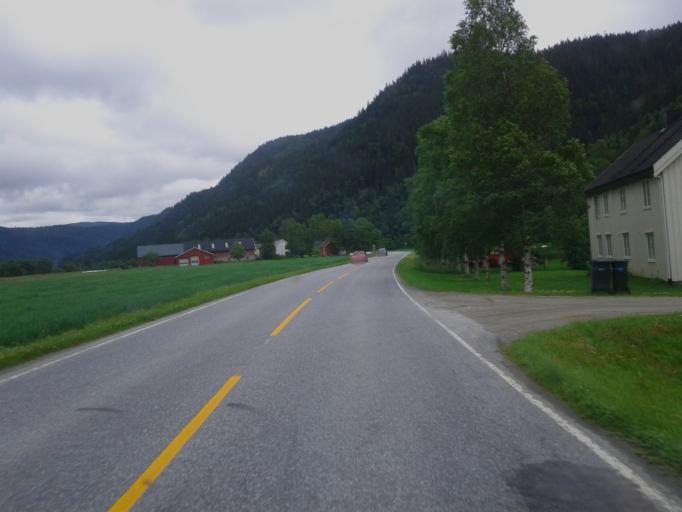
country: NO
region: Sor-Trondelag
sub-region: Midtre Gauldal
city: Storen
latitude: 63.0140
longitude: 10.3595
